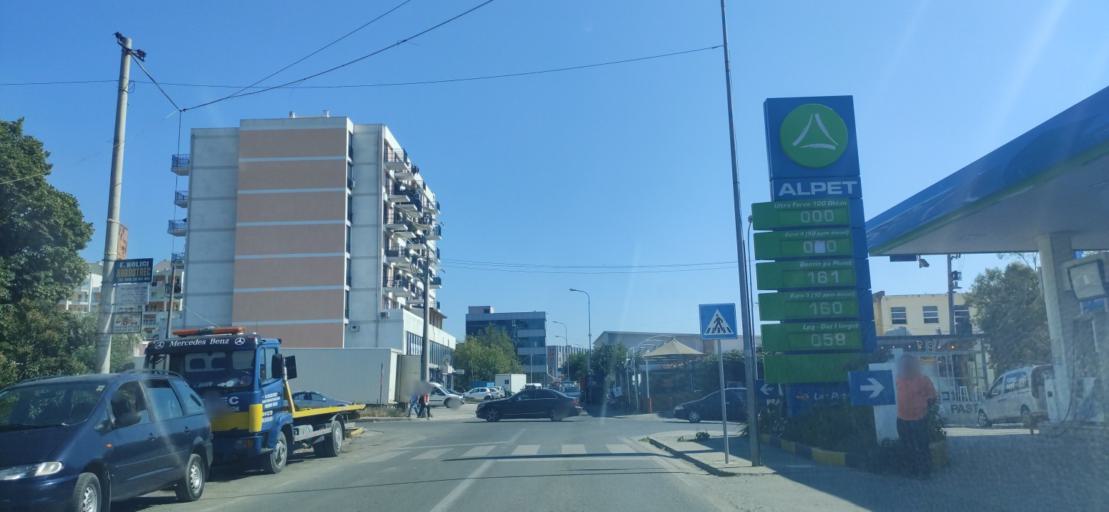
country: AL
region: Lezhe
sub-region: Rrethi i Kurbinit
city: Lac
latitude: 41.6366
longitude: 19.7115
